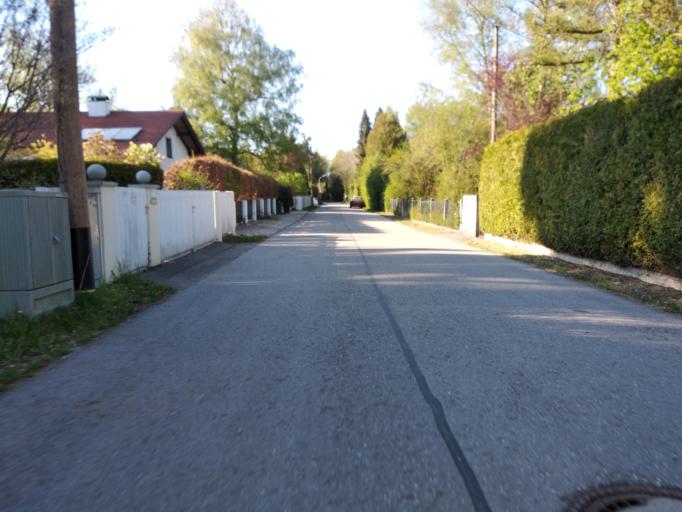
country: DE
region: Bavaria
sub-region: Upper Bavaria
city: Putzbrunn
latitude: 48.0646
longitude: 11.7289
